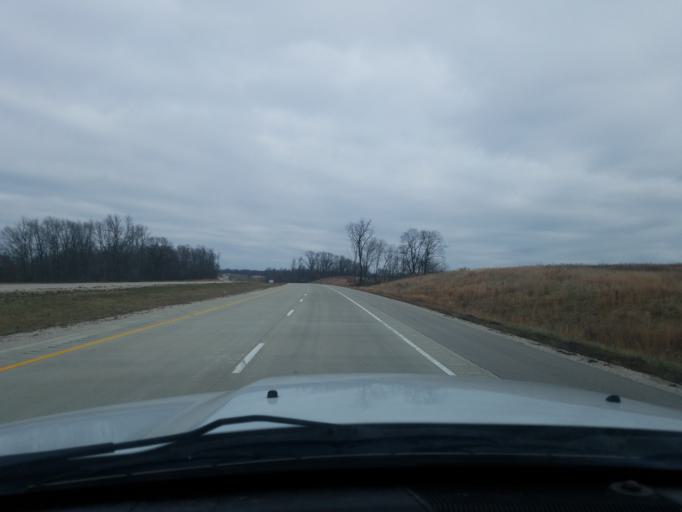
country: US
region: Indiana
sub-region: Greene County
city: Bloomfield
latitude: 38.9284
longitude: -86.8832
